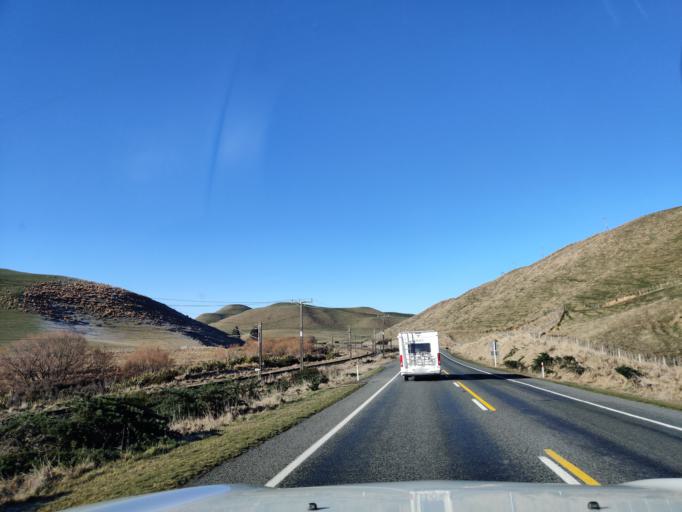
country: NZ
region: Manawatu-Wanganui
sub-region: Ruapehu District
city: Waiouru
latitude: -39.5022
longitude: 175.6739
